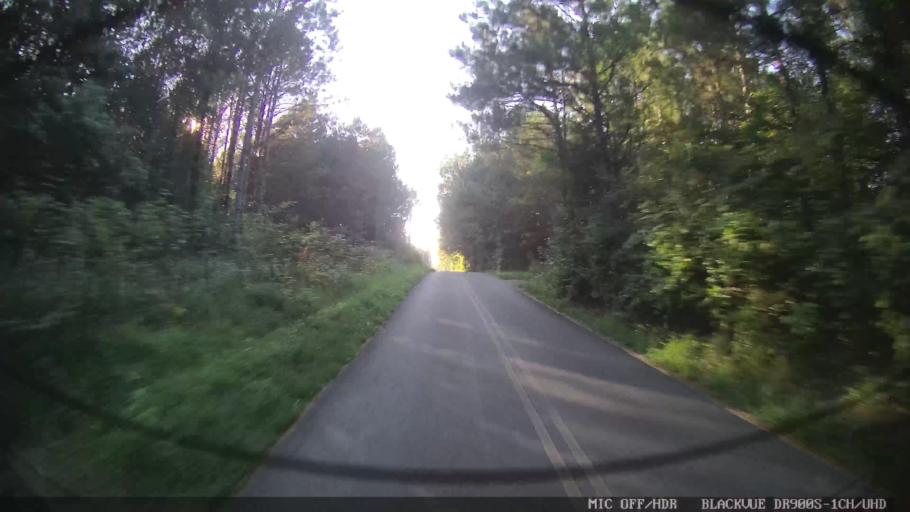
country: US
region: Tennessee
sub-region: Bradley County
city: Wildwood Lake
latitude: 35.0208
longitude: -84.7650
